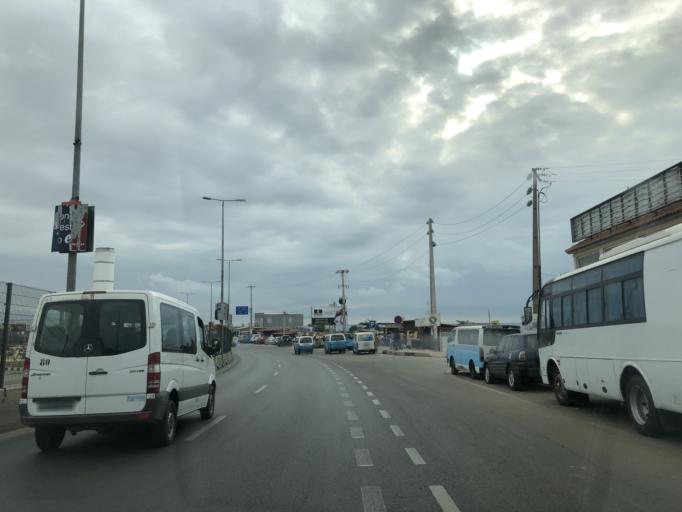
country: AO
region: Luanda
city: Luanda
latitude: -8.8506
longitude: 13.2222
